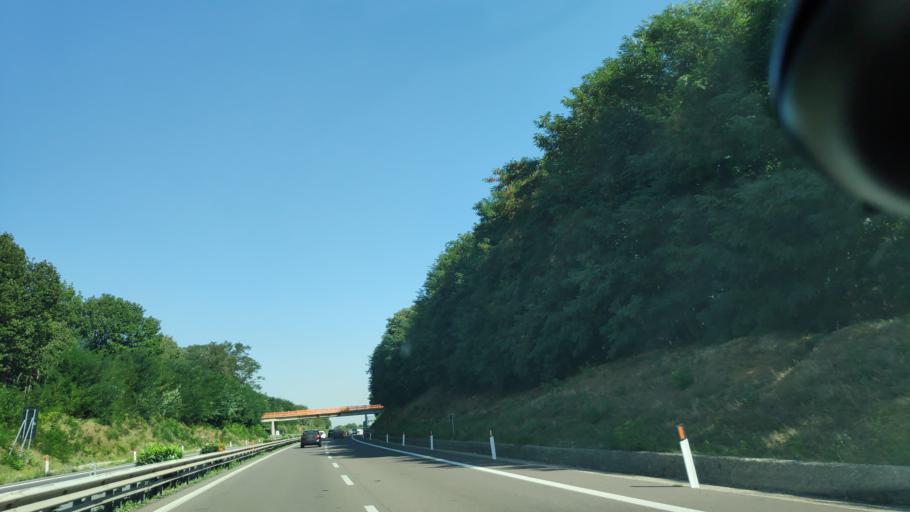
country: IT
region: Calabria
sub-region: Provincia di Cosenza
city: Piane Crati
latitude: 39.2148
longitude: 16.3061
